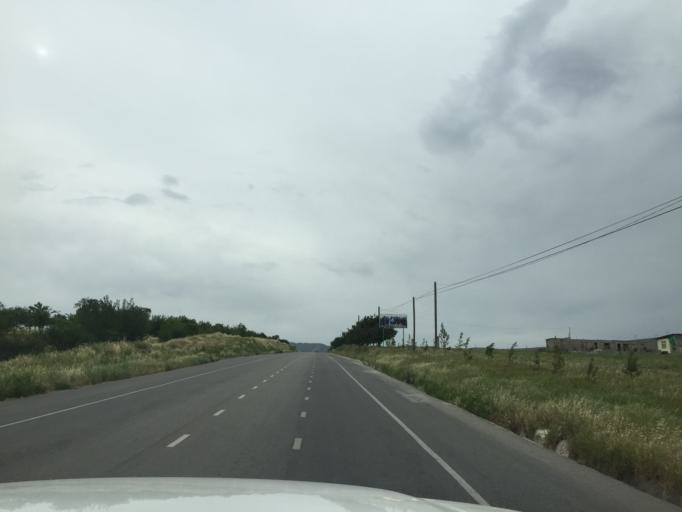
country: TJ
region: Republican Subordination
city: Vahdat
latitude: 38.5093
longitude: 69.1137
